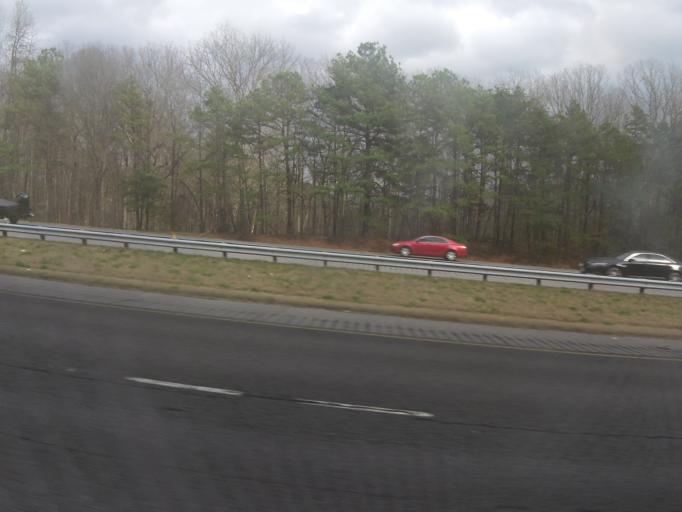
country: US
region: Georgia
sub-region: Whitfield County
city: Dalton
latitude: 34.7095
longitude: -85.0074
